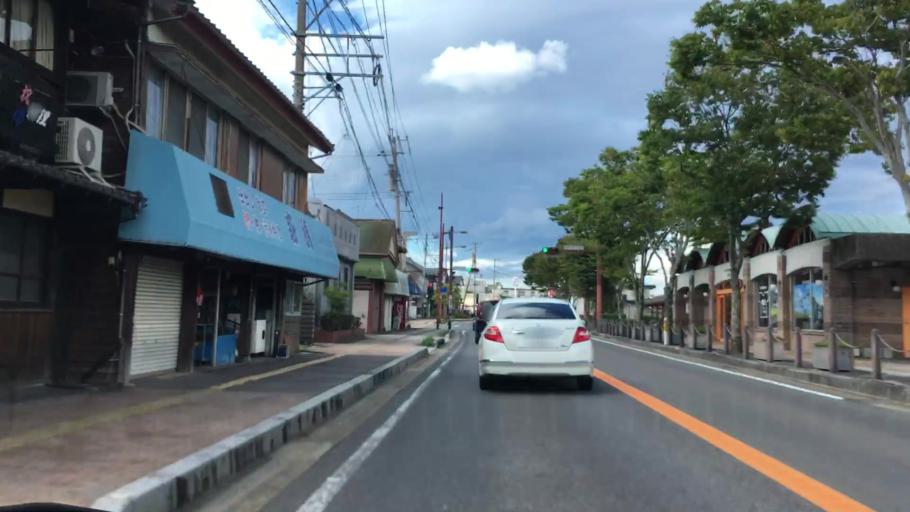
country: JP
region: Saga Prefecture
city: Imaricho-ko
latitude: 33.2098
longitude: 129.8499
